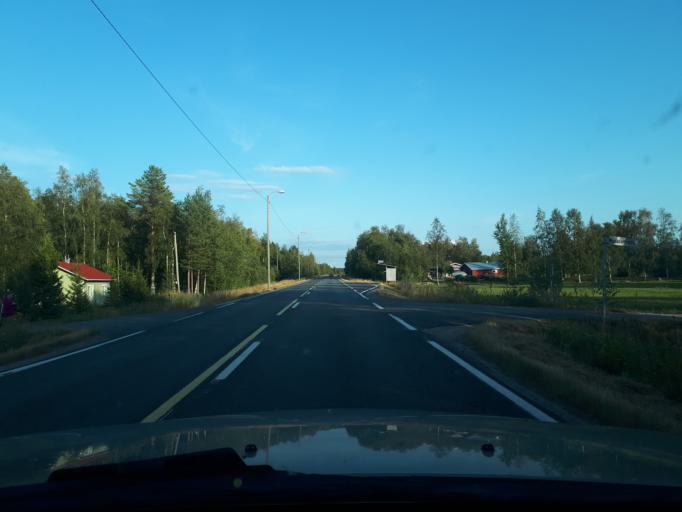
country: FI
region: Northern Ostrobothnia
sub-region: Oulu
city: Oulunsalo
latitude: 64.9857
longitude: 25.2631
